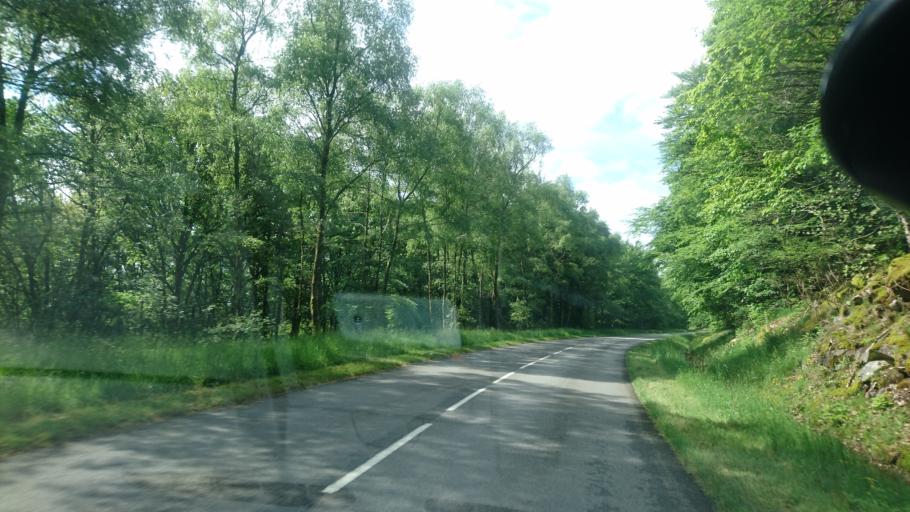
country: FR
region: Limousin
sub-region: Departement de la Haute-Vienne
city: Peyrat-le-Chateau
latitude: 45.7902
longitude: 1.8511
